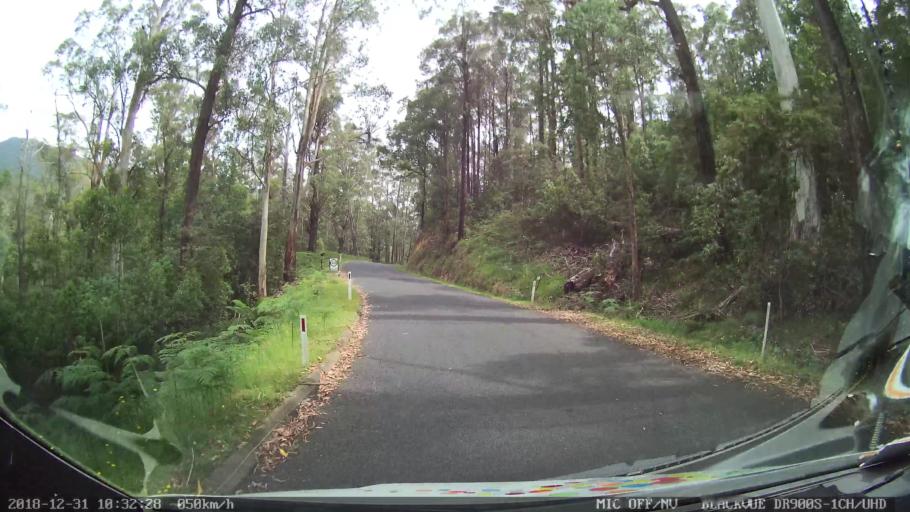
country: AU
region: New South Wales
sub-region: Snowy River
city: Jindabyne
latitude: -36.4506
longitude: 148.1612
